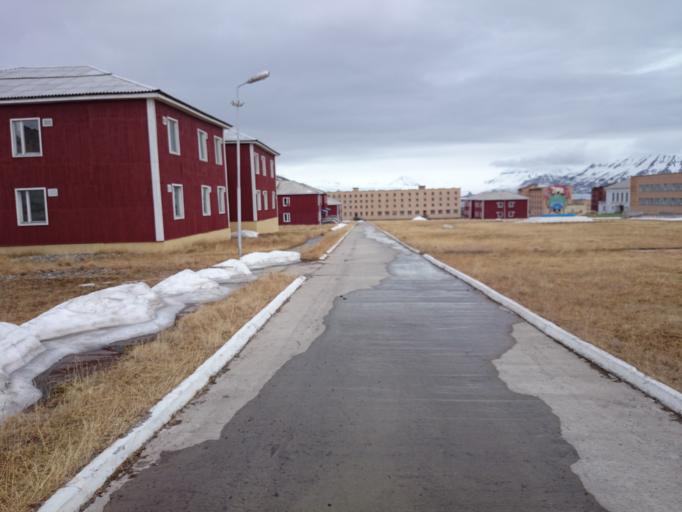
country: SJ
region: Svalbard
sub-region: Spitsbergen
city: Longyearbyen
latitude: 78.6559
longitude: 16.3138
